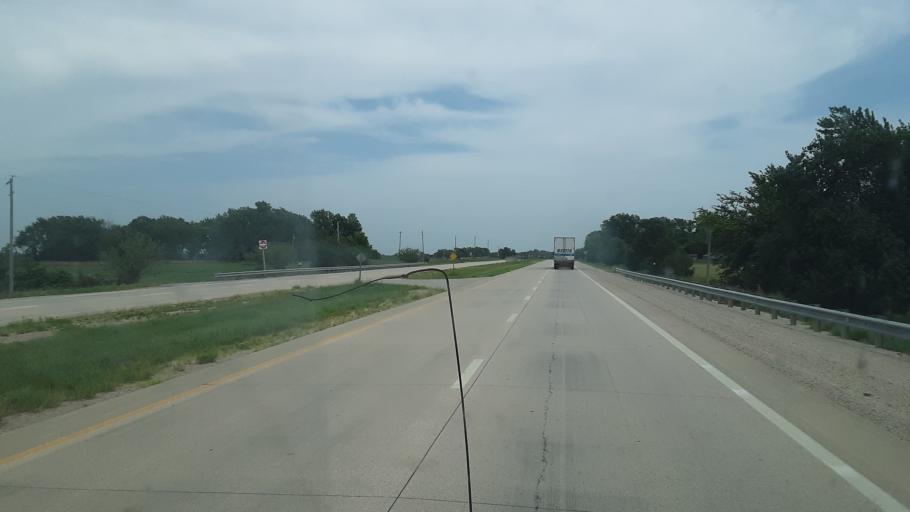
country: US
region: Kansas
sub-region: Allen County
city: Iola
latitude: 37.9220
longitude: -95.3272
